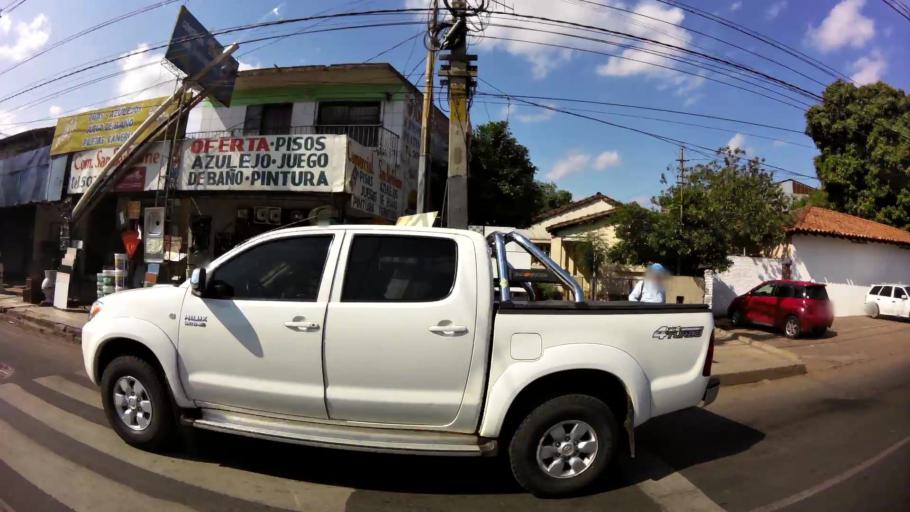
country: PY
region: Central
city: Fernando de la Mora
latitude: -25.3324
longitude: -57.5399
